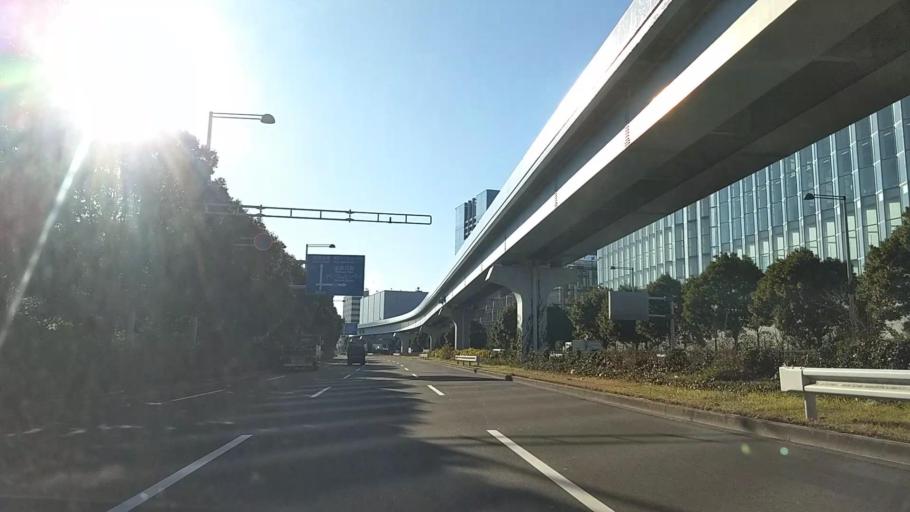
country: JP
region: Tokyo
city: Tokyo
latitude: 35.6212
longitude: 139.7794
